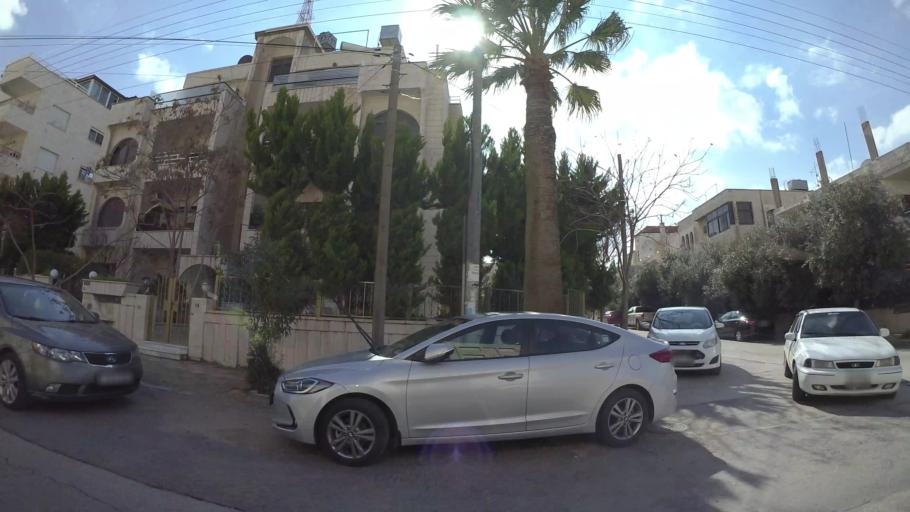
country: JO
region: Amman
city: Amman
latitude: 31.9772
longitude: 35.8951
